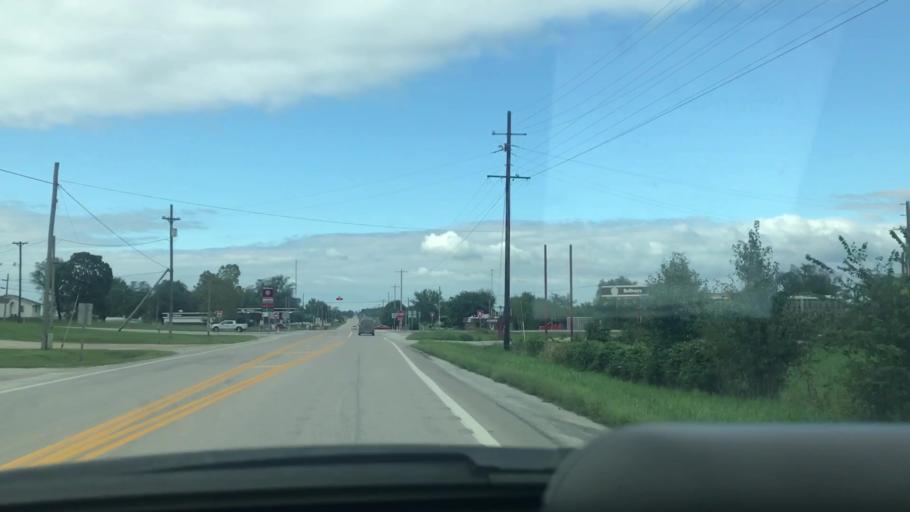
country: US
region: Missouri
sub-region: Hickory County
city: Hermitage
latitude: 37.9397
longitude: -93.2081
